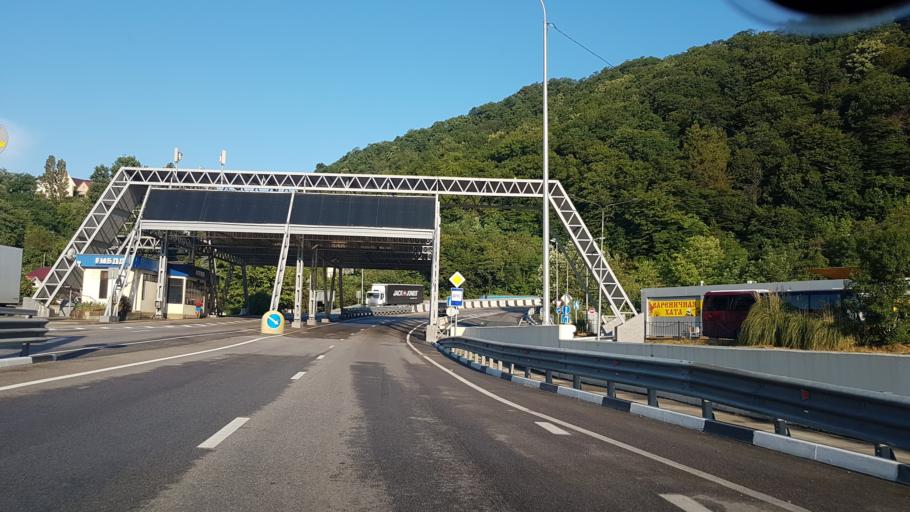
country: RU
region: Krasnodarskiy
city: Dagomys
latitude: 43.6395
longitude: 39.6999
